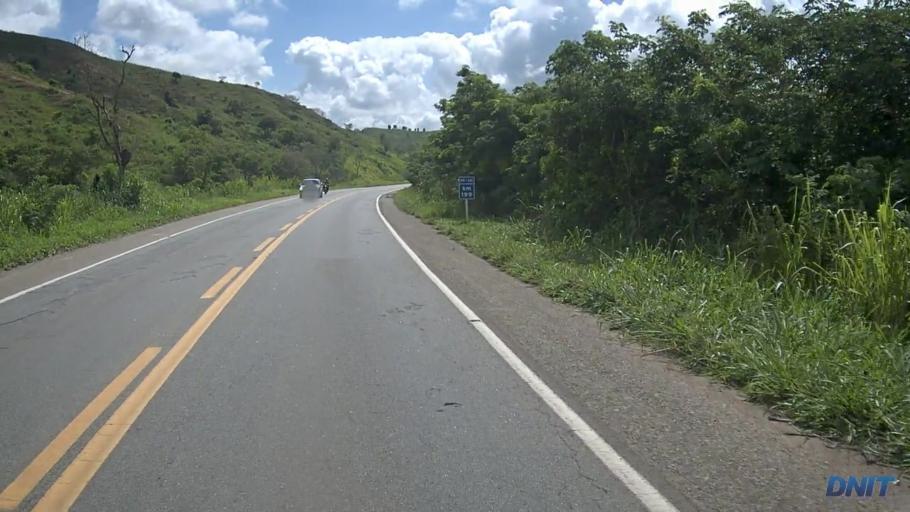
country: BR
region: Minas Gerais
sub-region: Belo Oriente
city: Belo Oriente
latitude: -19.1395
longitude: -42.2206
